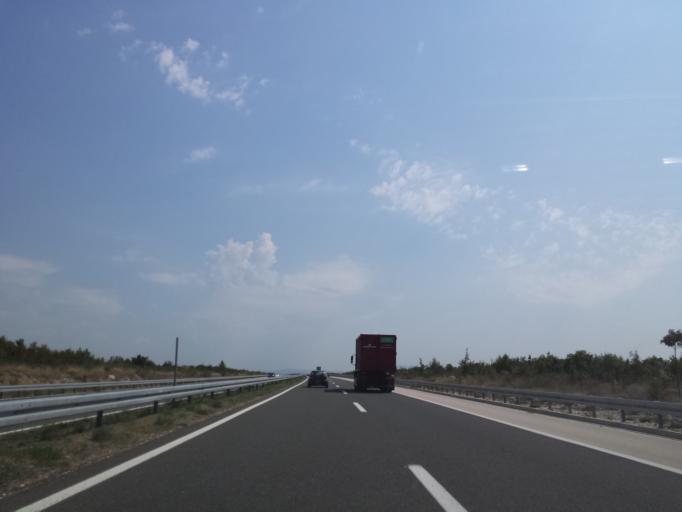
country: HR
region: Sibensko-Kniniska
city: Zaton
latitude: 43.8653
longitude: 15.8168
